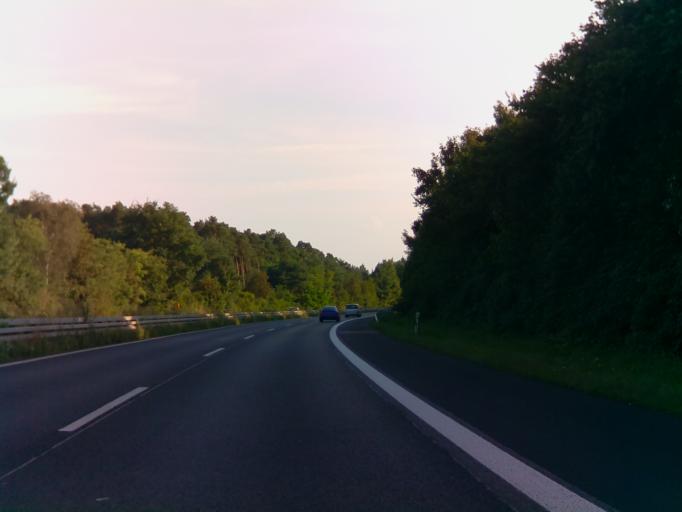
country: DE
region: Hesse
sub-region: Regierungsbezirk Darmstadt
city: Rodgau
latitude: 50.0050
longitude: 8.8977
